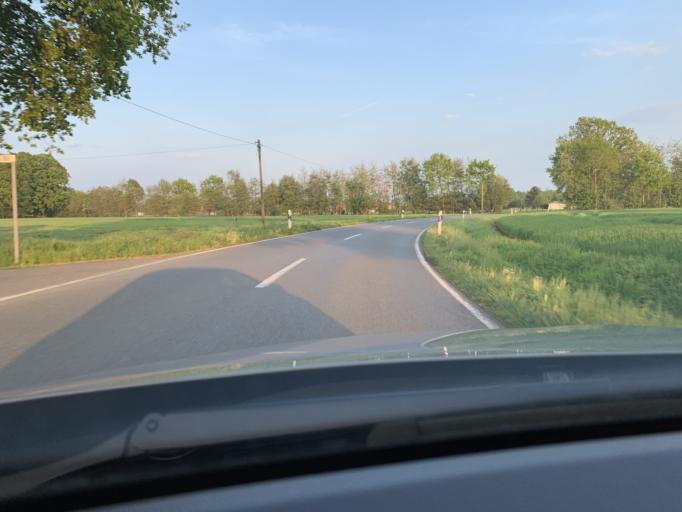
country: DE
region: North Rhine-Westphalia
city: Rietberg
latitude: 51.7948
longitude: 8.4016
